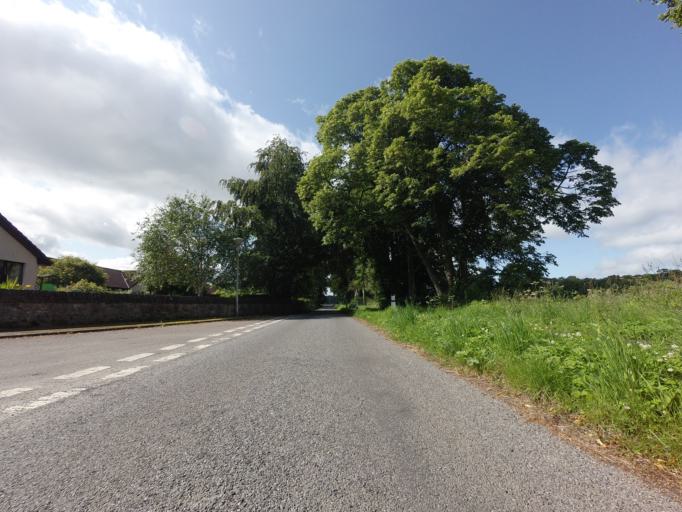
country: GB
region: Scotland
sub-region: Highland
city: Nairn
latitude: 57.5746
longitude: -3.8627
